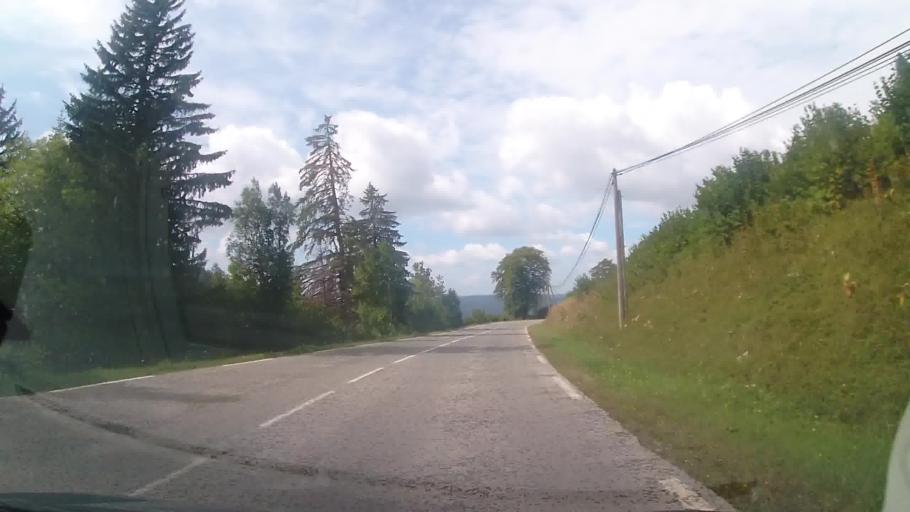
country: FR
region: Franche-Comte
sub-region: Departement du Jura
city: Les Rousses
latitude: 46.4513
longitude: 6.0716
